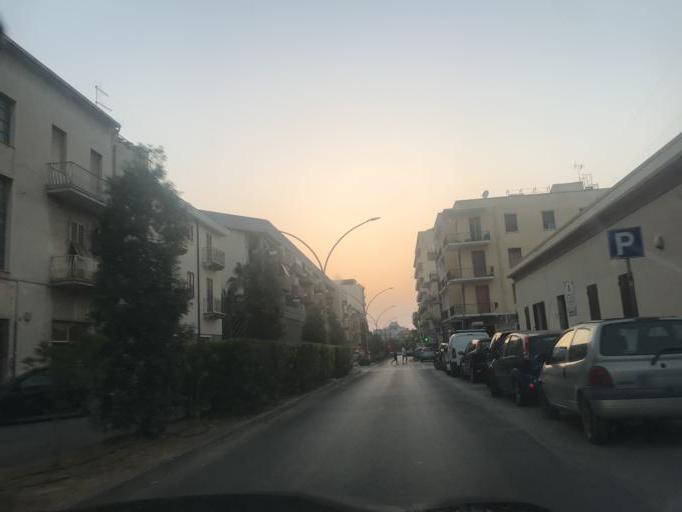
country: IT
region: Sardinia
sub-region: Provincia di Sassari
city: Alghero
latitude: 40.5542
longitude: 8.3218
